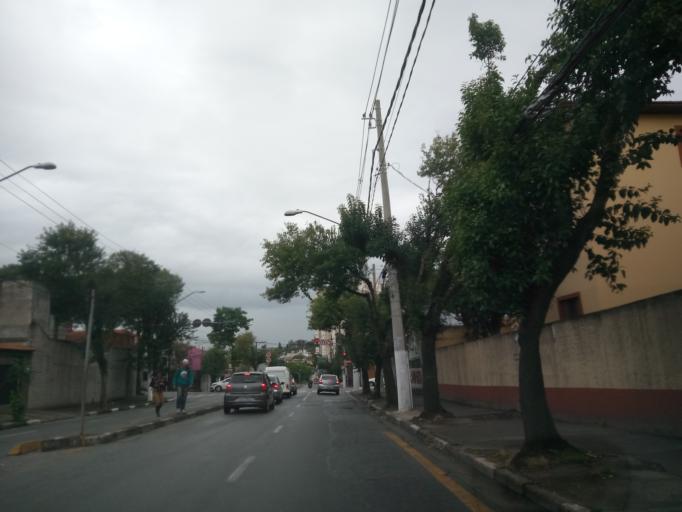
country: BR
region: Sao Paulo
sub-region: Sao Bernardo Do Campo
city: Sao Bernardo do Campo
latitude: -23.7285
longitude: -46.5727
